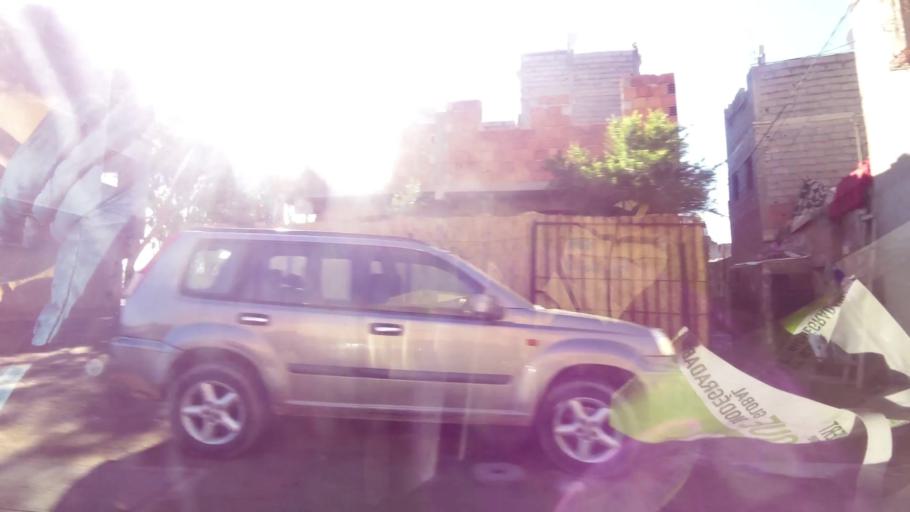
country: MA
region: Marrakech-Tensift-Al Haouz
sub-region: Marrakech
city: Marrakesh
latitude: 31.6007
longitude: -8.0310
